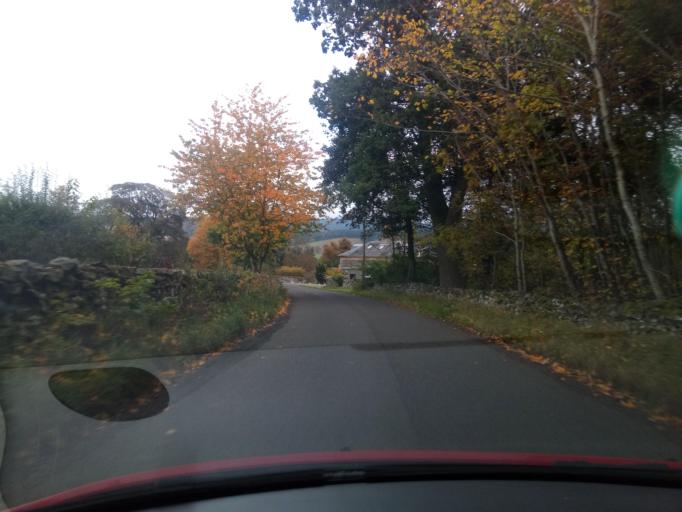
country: GB
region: Scotland
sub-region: The Scottish Borders
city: Peebles
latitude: 55.6373
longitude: -3.1479
